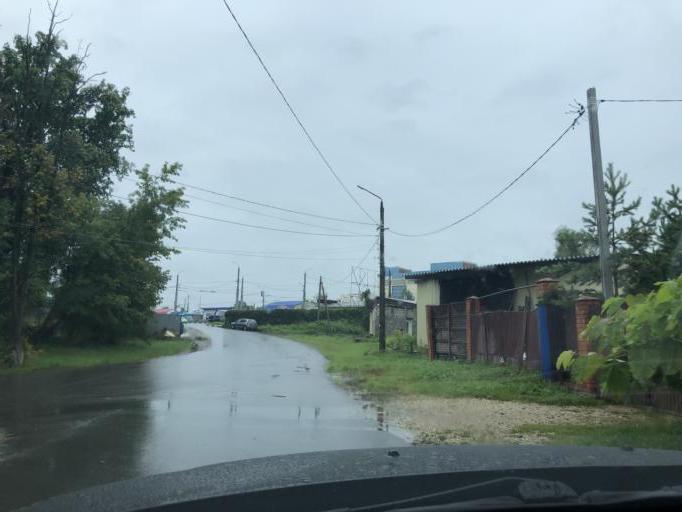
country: RU
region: Tula
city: Gorelki
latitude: 54.2539
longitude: 37.6105
